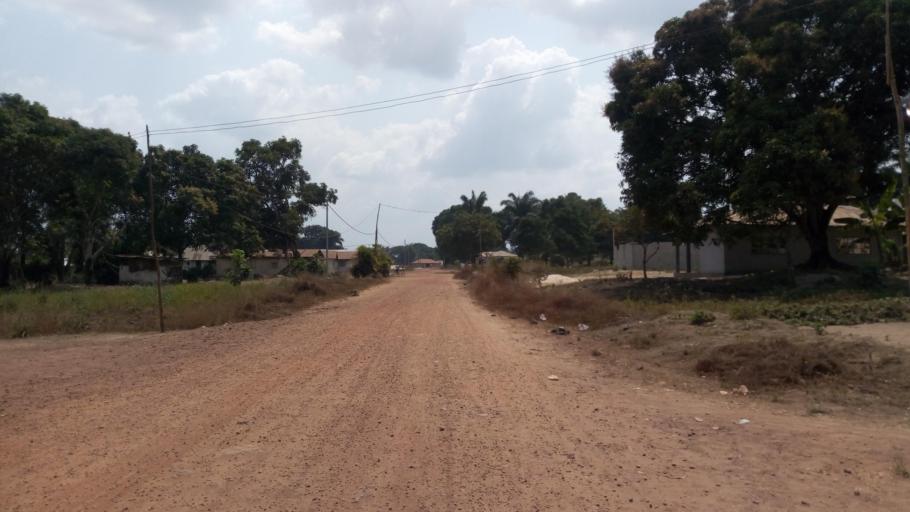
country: SL
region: Southern Province
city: Mogbwemo
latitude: 7.7920
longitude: -12.3018
